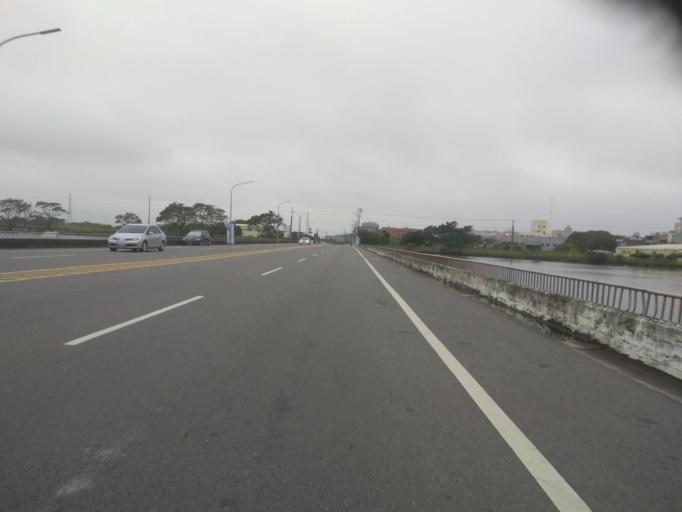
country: TW
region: Taiwan
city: Taoyuan City
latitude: 25.0118
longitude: 121.1352
